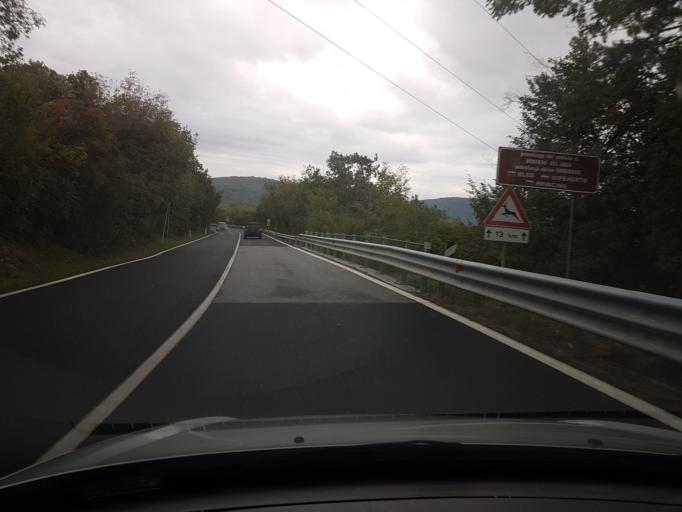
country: IT
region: Friuli Venezia Giulia
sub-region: Provincia di Gorizia
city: Monfalcone
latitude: 45.8103
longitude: 13.5800
